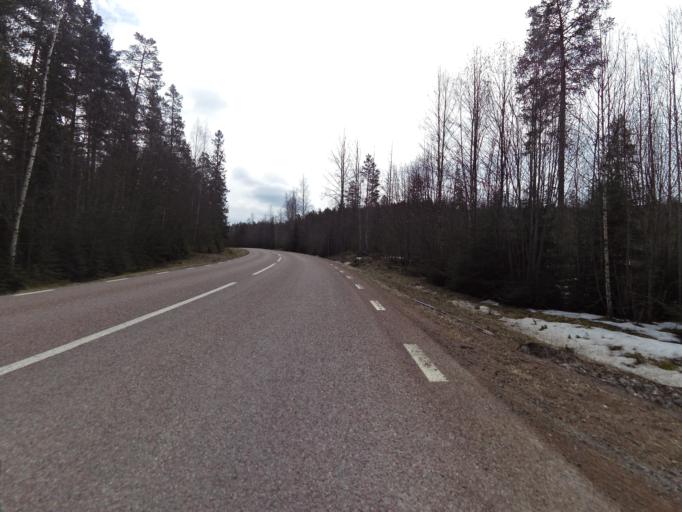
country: SE
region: Dalarna
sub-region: Hedemora Kommun
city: Langshyttan
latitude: 60.5438
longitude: 16.1233
